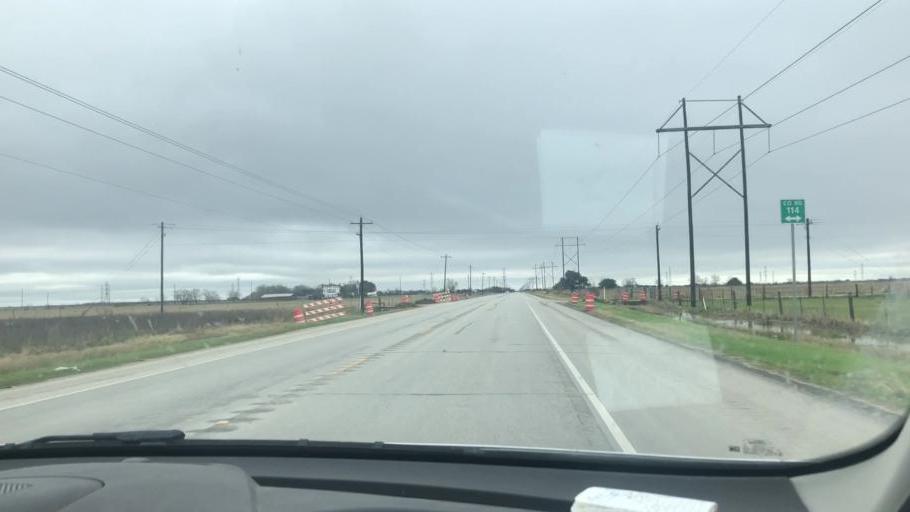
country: US
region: Texas
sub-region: Wharton County
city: Boling
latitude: 29.1865
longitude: -96.0118
